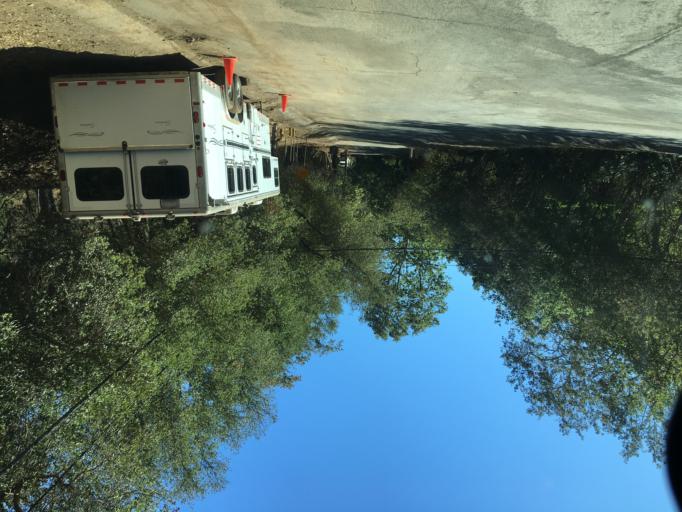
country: US
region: California
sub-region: Los Angeles County
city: Malibu
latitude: 34.0516
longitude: -118.7761
